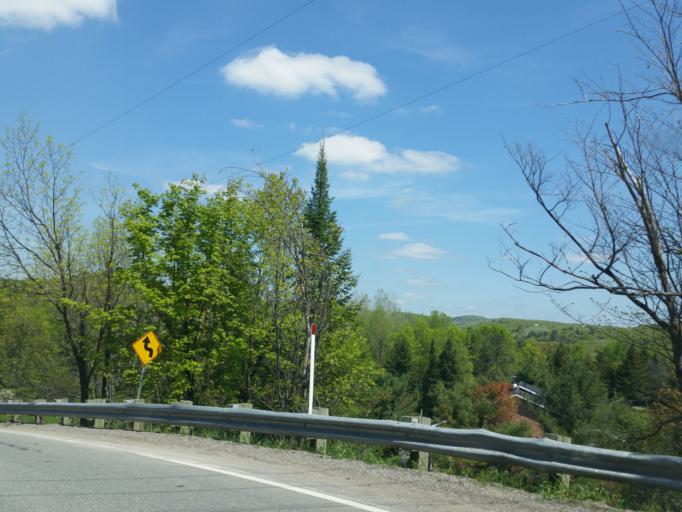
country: CA
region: Quebec
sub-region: Outaouais
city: Wakefield
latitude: 45.5789
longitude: -75.8716
